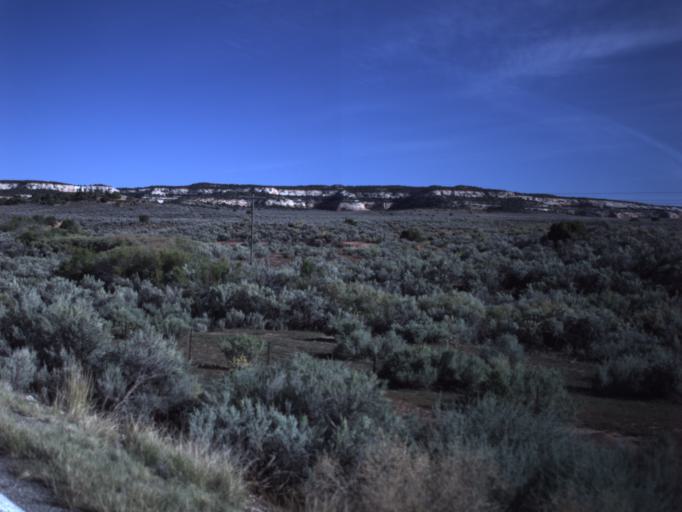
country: US
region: Utah
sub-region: Grand County
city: Moab
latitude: 38.3044
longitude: -109.3861
